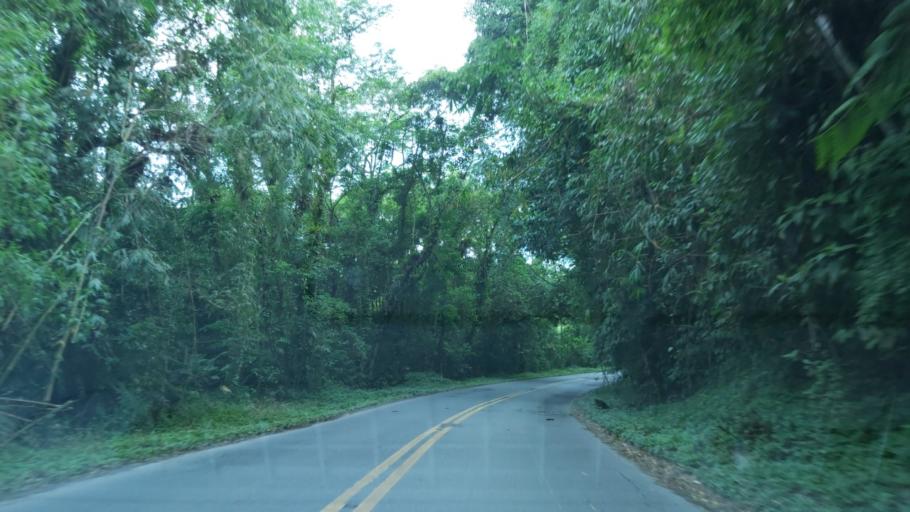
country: BR
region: Sao Paulo
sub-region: Miracatu
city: Miracatu
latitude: -24.0693
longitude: -47.5992
